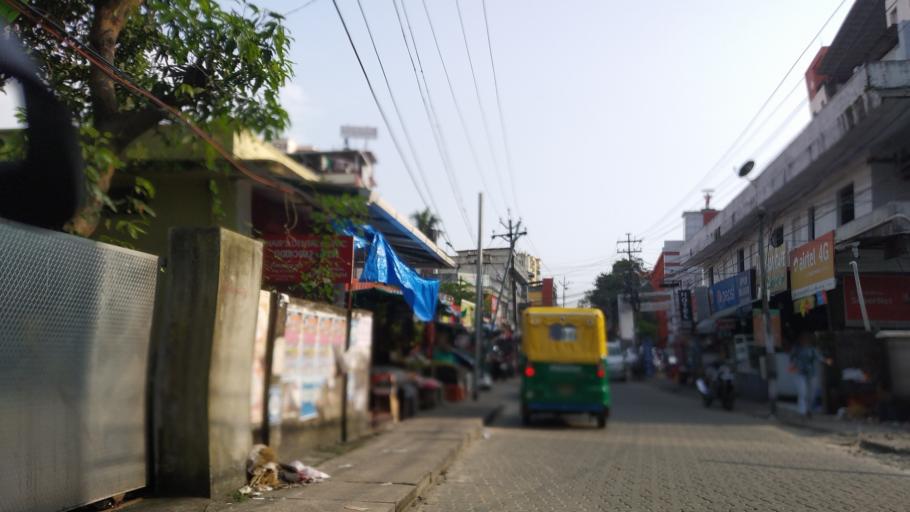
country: IN
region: Kerala
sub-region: Ernakulam
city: Cochin
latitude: 9.9894
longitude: 76.2885
